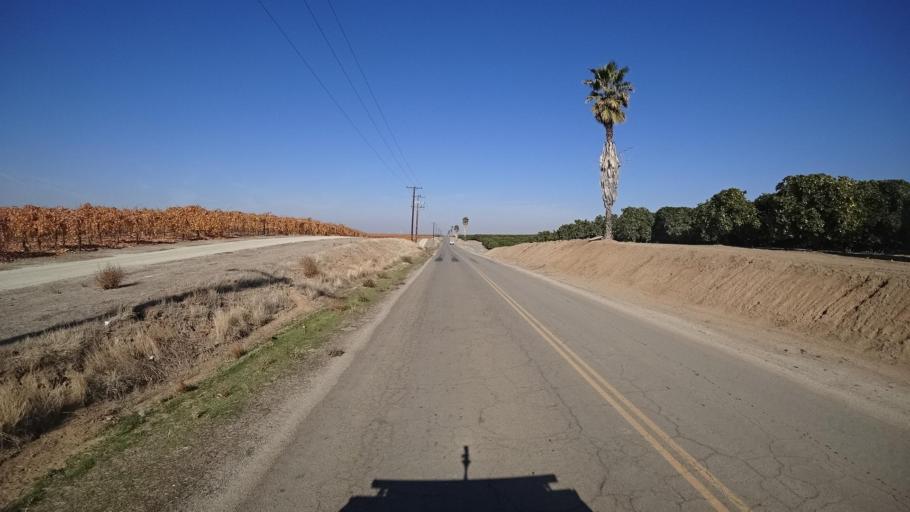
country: US
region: California
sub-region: Tulare County
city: Richgrove
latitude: 35.7055
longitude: -119.1337
